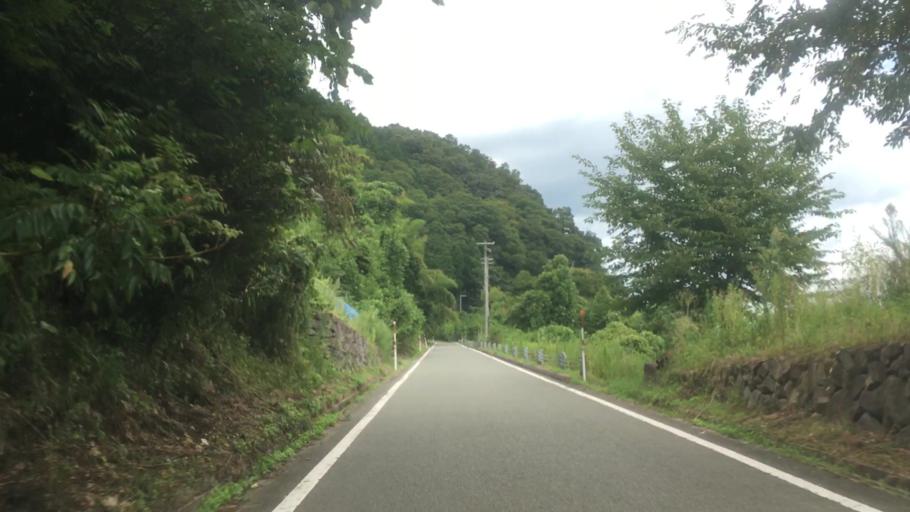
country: JP
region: Hyogo
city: Toyooka
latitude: 35.5816
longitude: 134.7991
